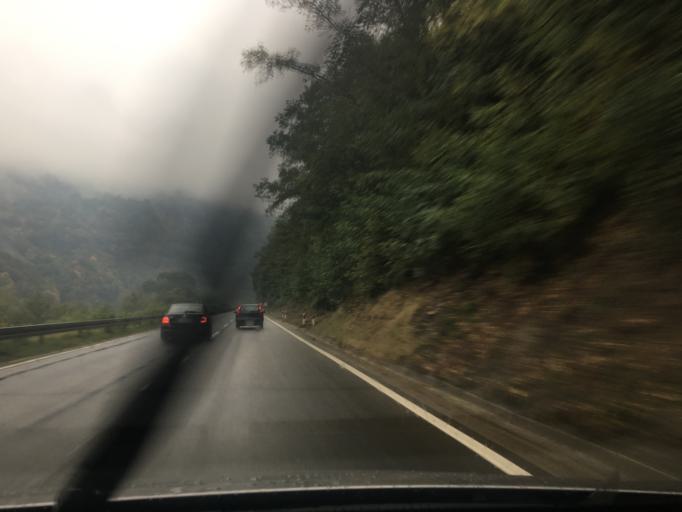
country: RS
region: Central Serbia
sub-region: Pcinjski Okrug
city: Vladicin Han
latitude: 42.7330
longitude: 22.0640
